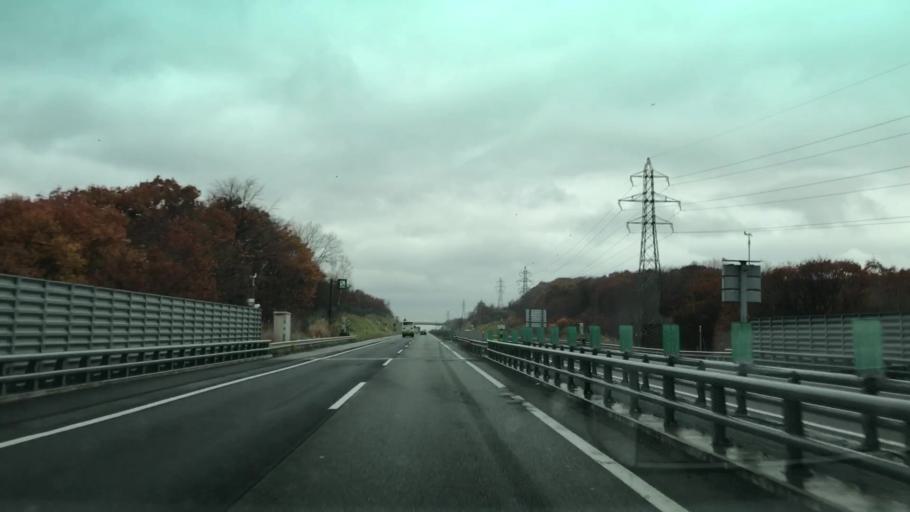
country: JP
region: Hokkaido
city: Kitahiroshima
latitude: 42.9586
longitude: 141.5032
